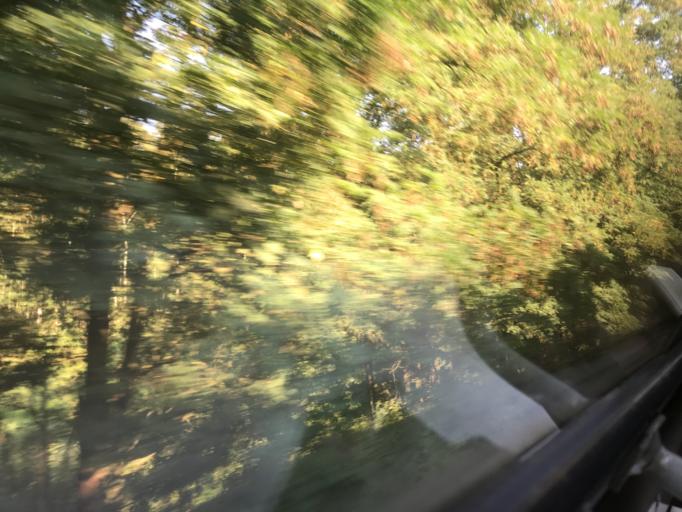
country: CZ
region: Jihocesky
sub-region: Okres Tabor
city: Veseli nad Luznici
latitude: 49.1456
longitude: 14.7299
